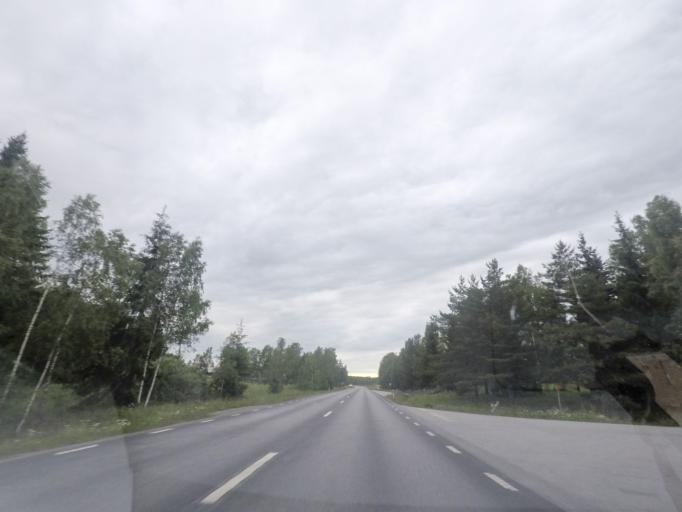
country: SE
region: OErebro
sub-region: Lindesbergs Kommun
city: Lindesberg
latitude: 59.5428
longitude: 15.2476
